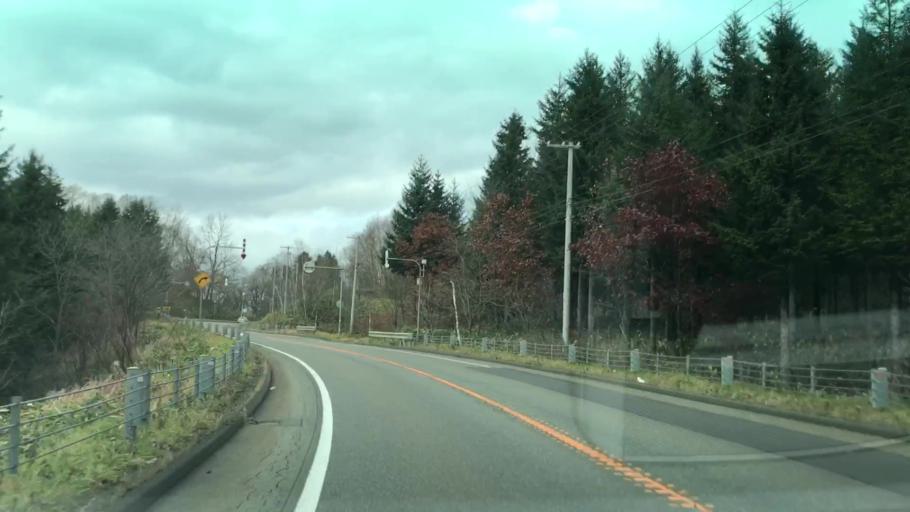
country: JP
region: Hokkaido
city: Shimo-furano
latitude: 42.8896
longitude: 142.4365
